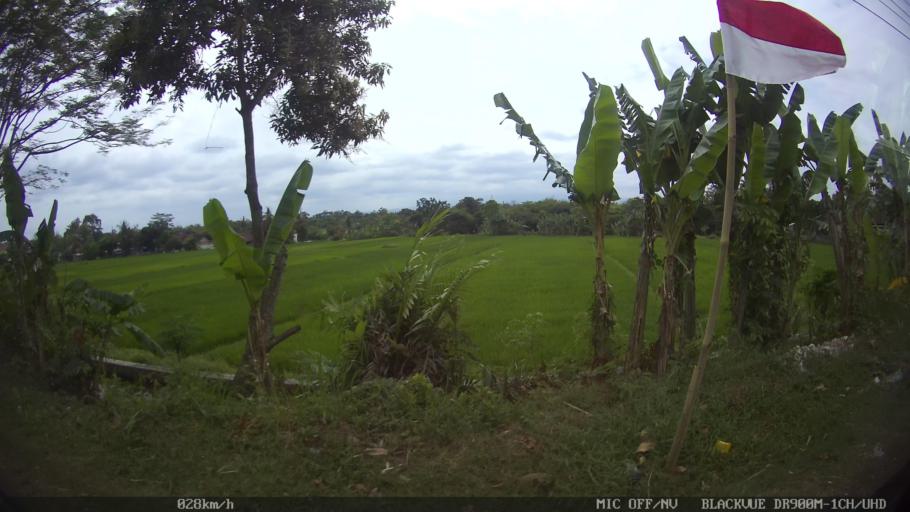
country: ID
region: Central Java
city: Candi Prambanan
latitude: -7.7697
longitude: 110.4844
